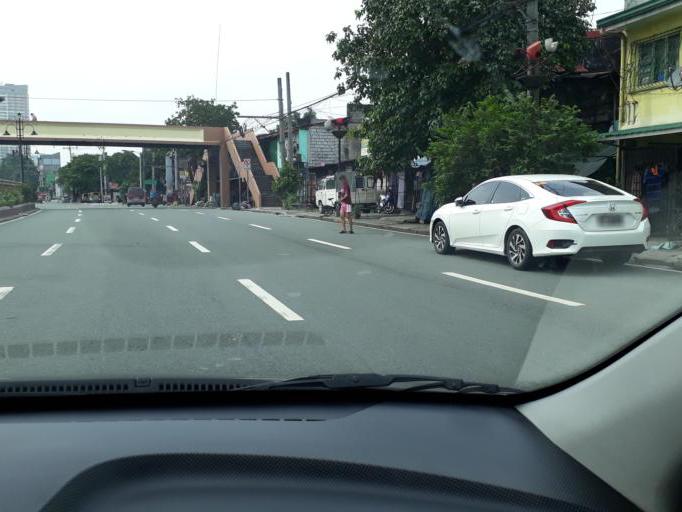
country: PH
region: Metro Manila
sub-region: City of Manila
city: Quiapo
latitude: 14.6043
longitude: 120.9977
